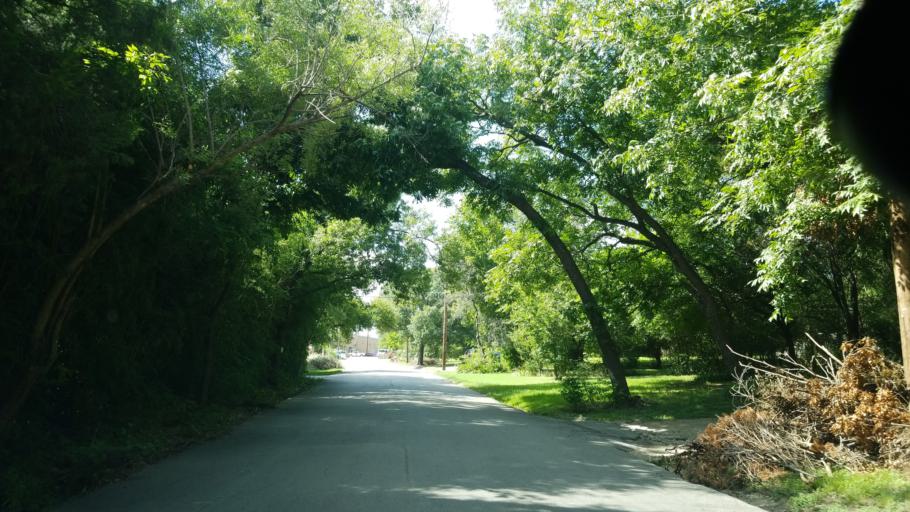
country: US
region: Texas
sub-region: Dallas County
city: Balch Springs
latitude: 32.7693
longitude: -96.6956
